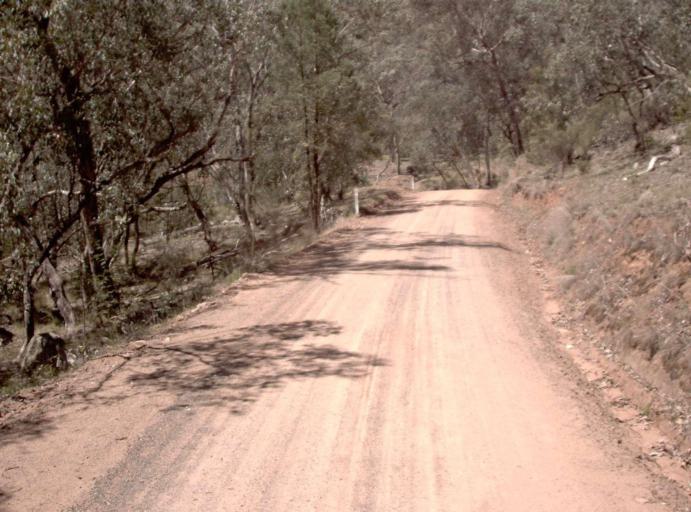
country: AU
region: New South Wales
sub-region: Snowy River
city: Jindabyne
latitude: -37.0541
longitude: 148.5379
